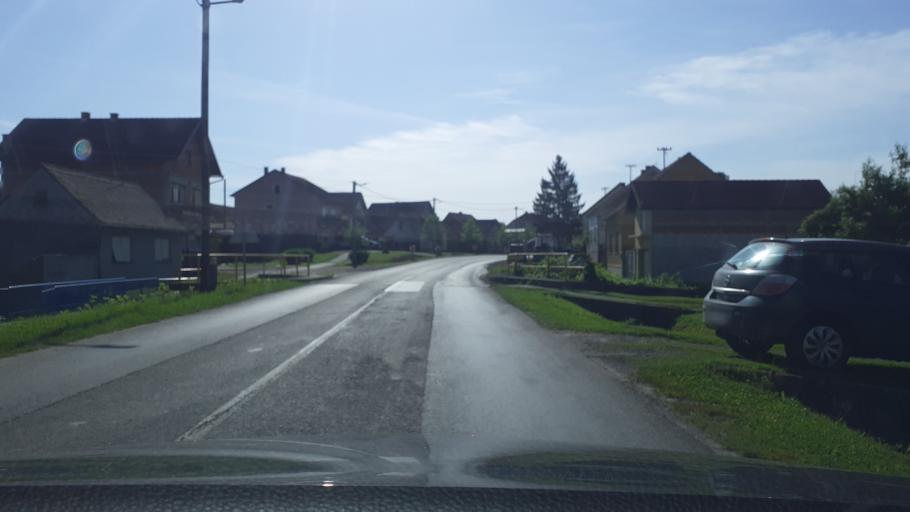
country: HR
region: Brodsko-Posavska
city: Batrina
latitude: 45.1938
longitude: 17.6521
